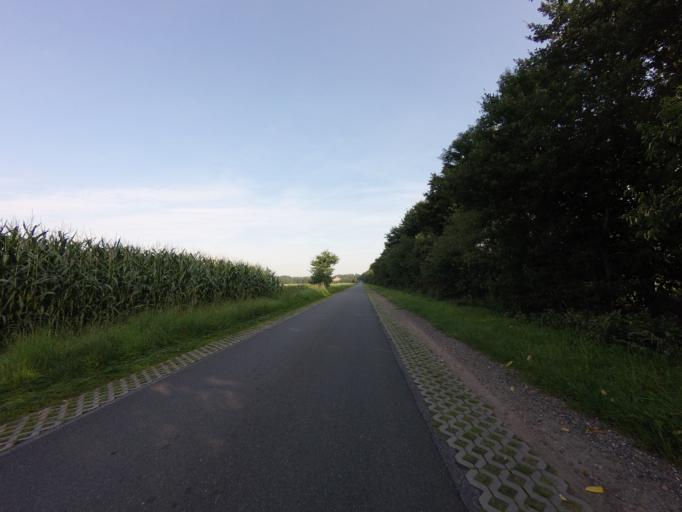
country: DE
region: Lower Saxony
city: Itterbeck
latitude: 52.4818
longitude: 6.8186
